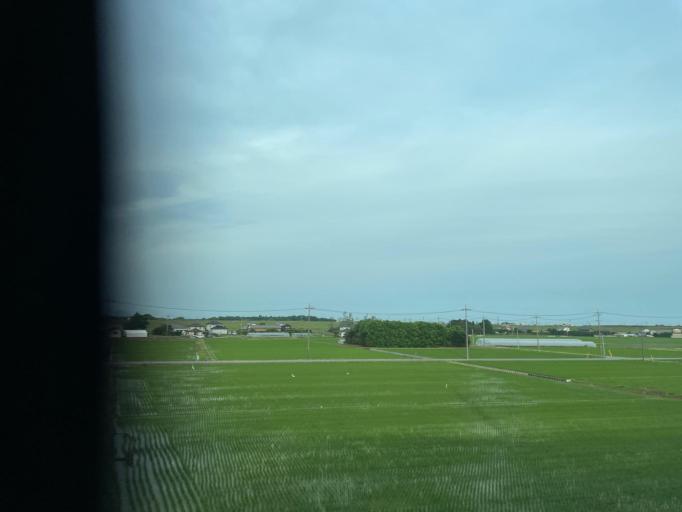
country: JP
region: Ibaraki
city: Koga
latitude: 36.1684
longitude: 139.6854
